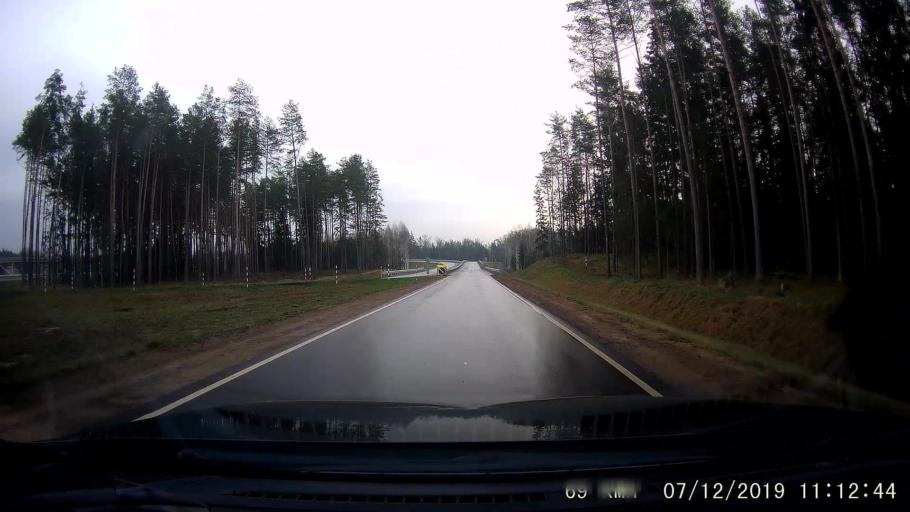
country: BY
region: Grodnenskaya
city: Iwye
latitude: 53.8819
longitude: 25.7354
